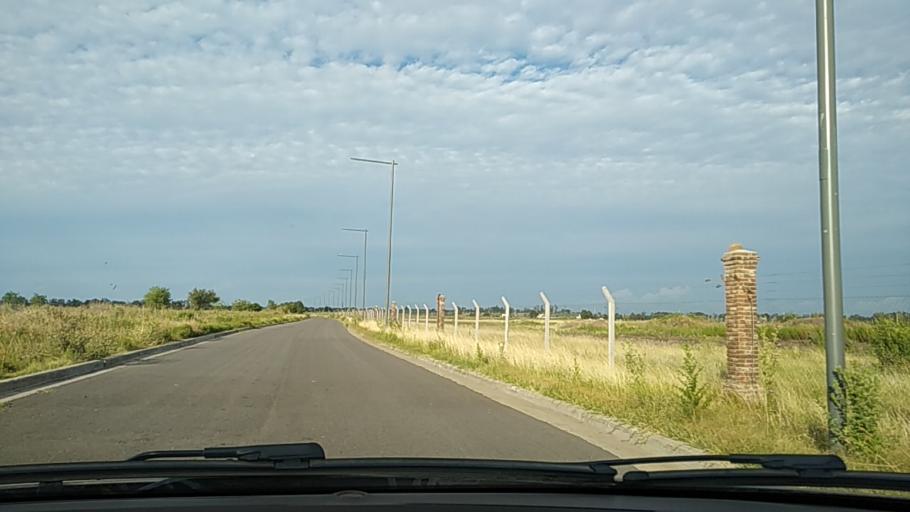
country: AR
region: Santa Fe
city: Funes
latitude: -32.9446
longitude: -60.7767
